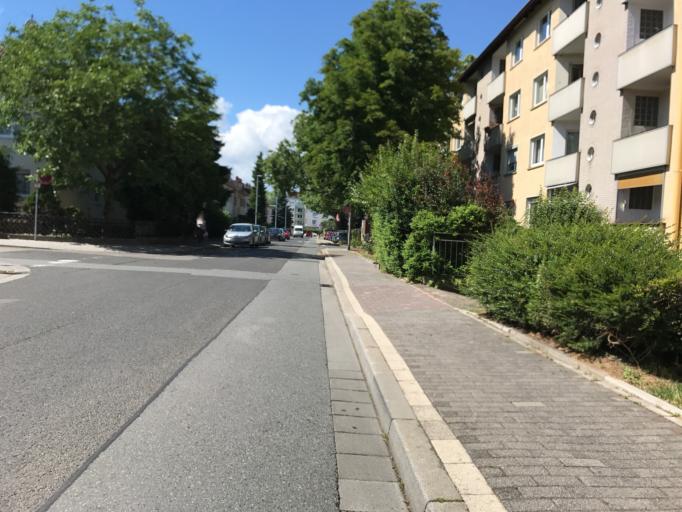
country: DE
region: Rheinland-Pfalz
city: Mainz
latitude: 49.9780
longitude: 8.2942
